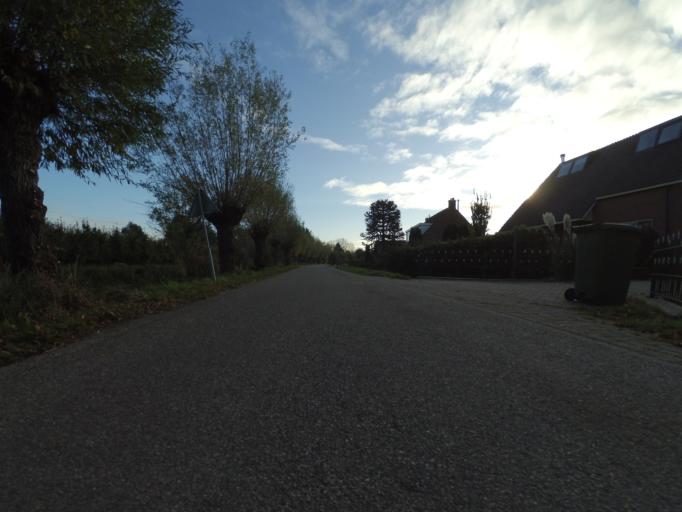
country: NL
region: Utrecht
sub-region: Gemeente Utrecht
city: Lunetten
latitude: 52.0498
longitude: 5.1311
